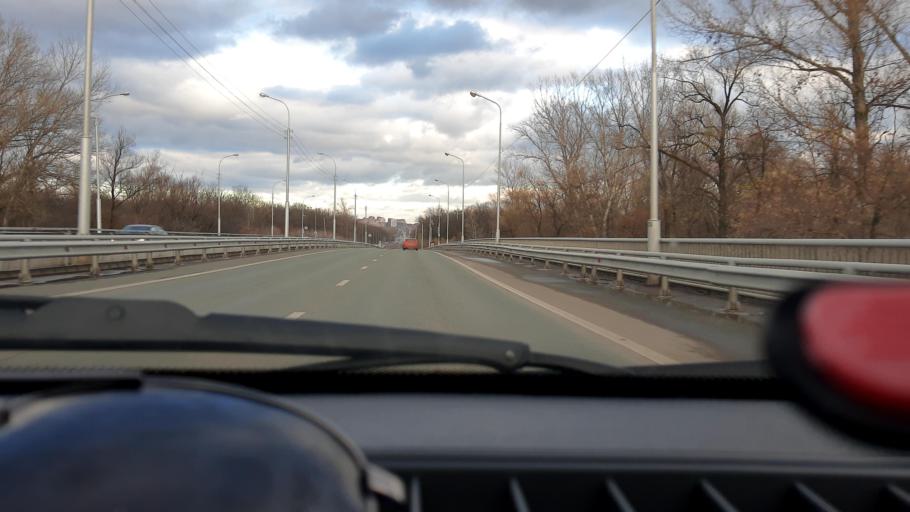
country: RU
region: Bashkortostan
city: Ufa
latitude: 54.7000
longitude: 55.9146
